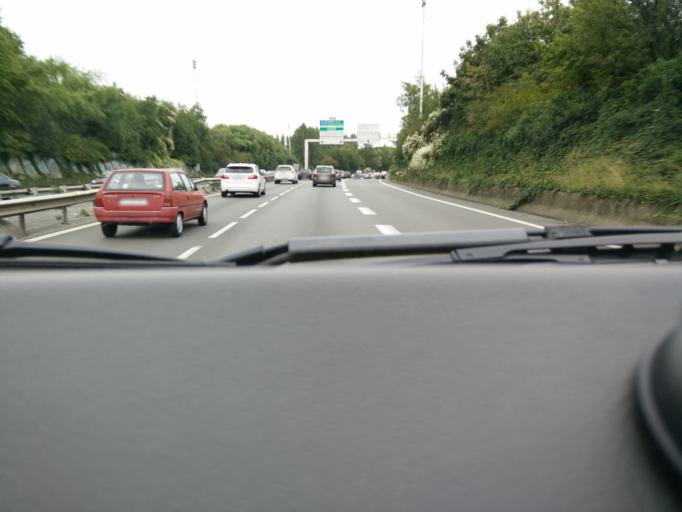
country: FR
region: Nord-Pas-de-Calais
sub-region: Departement du Nord
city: Mons-en-Baroeul
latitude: 50.6239
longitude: 3.1349
